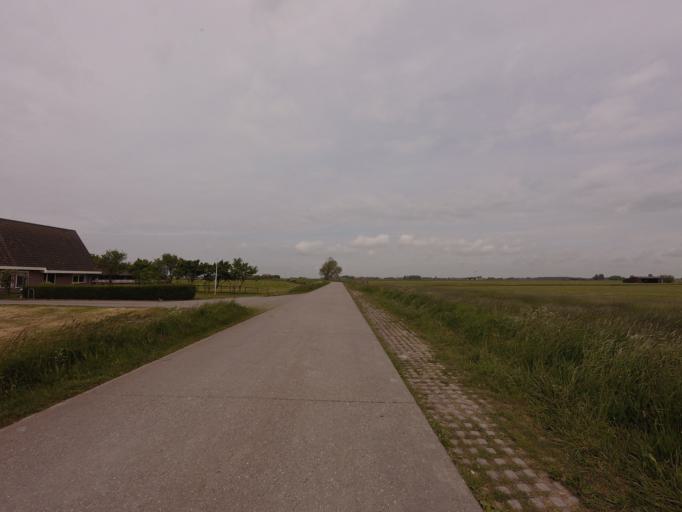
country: NL
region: Friesland
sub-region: Sudwest Fryslan
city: Makkum
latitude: 53.0648
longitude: 5.4602
